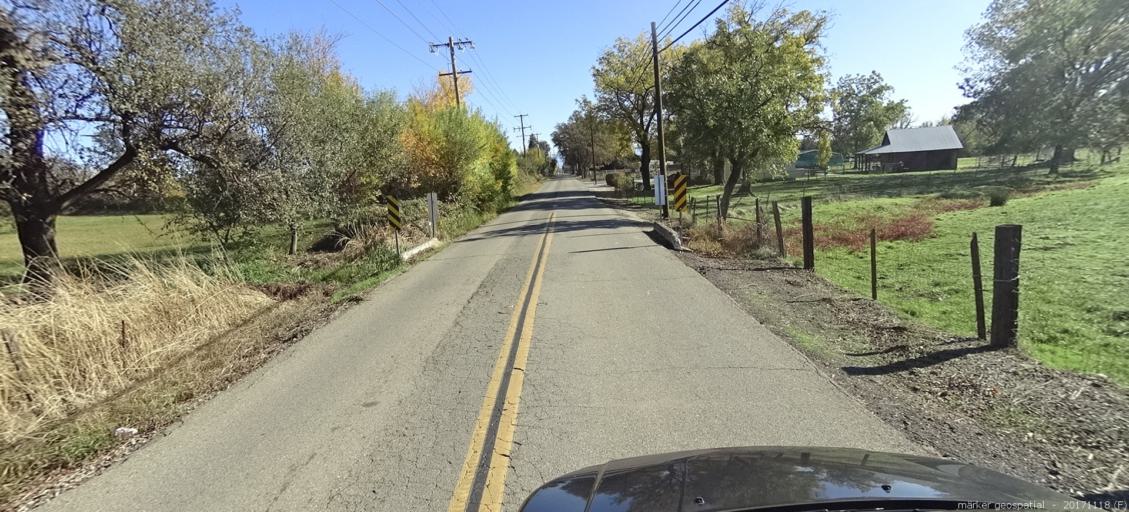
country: US
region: California
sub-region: Shasta County
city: Cottonwood
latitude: 40.3966
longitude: -122.2734
